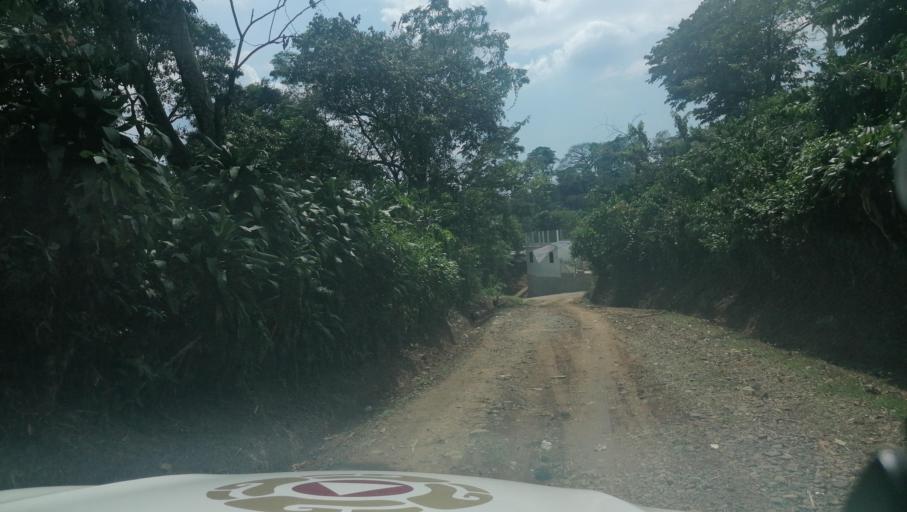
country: MX
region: Chiapas
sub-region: Cacahoatan
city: Benito Juarez
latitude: 15.0540
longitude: -92.2292
